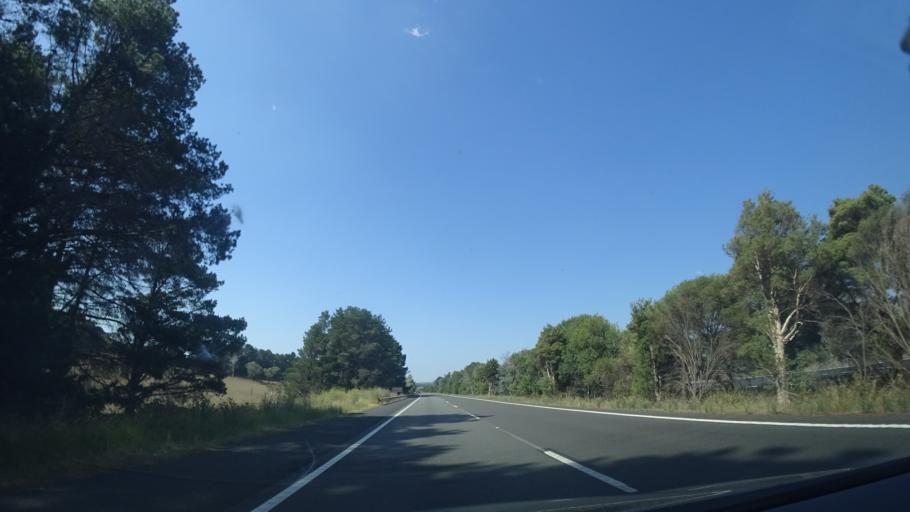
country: AU
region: New South Wales
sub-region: Wingecarribee
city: Moss Vale
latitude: -34.5544
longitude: 150.2641
